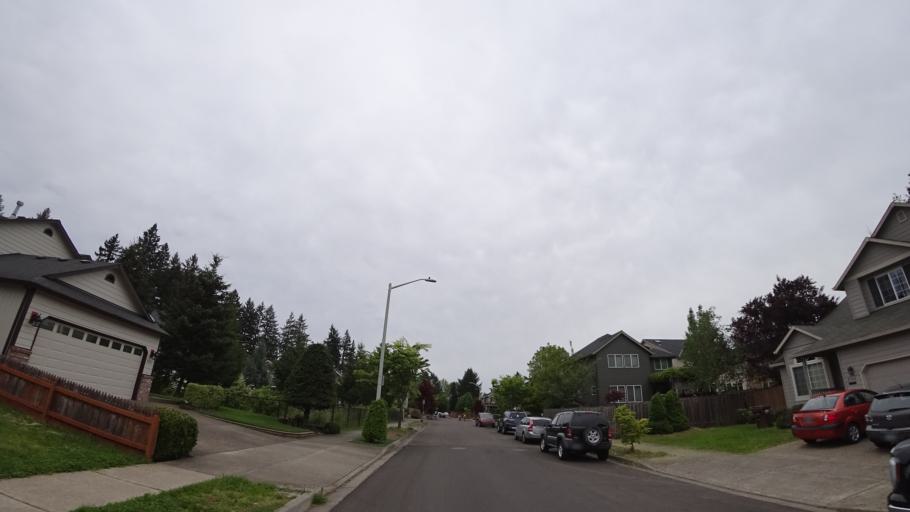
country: US
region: Oregon
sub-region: Washington County
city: Hillsboro
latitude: 45.5043
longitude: -122.9343
